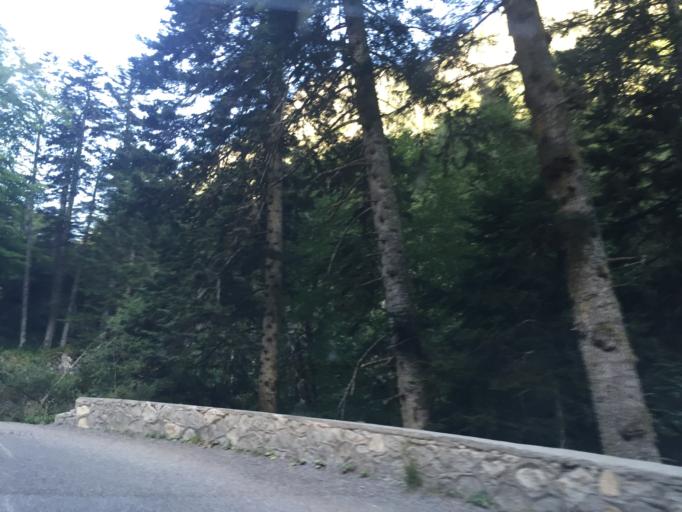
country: FR
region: Midi-Pyrenees
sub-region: Departement des Hautes-Pyrenees
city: Cauterets
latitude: 42.8636
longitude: -0.1184
